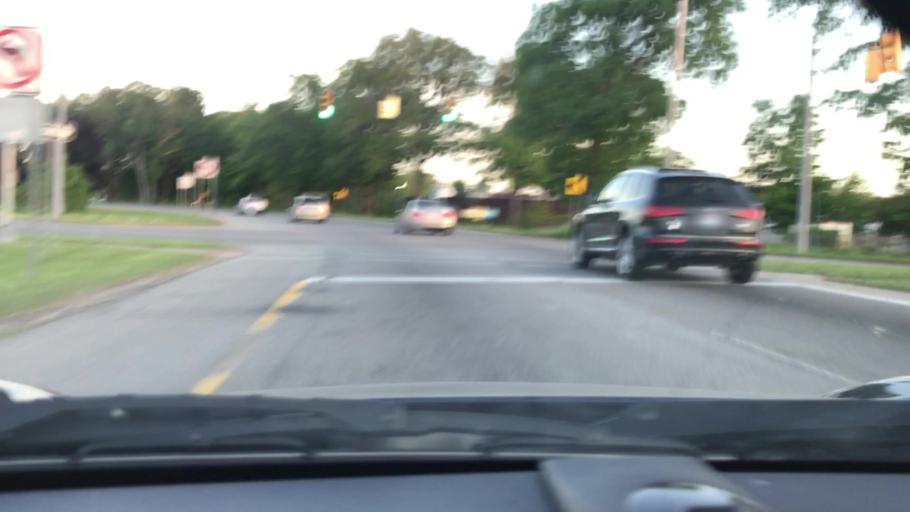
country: US
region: Michigan
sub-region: Muskegon County
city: Roosevelt Park
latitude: 43.1910
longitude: -86.2602
